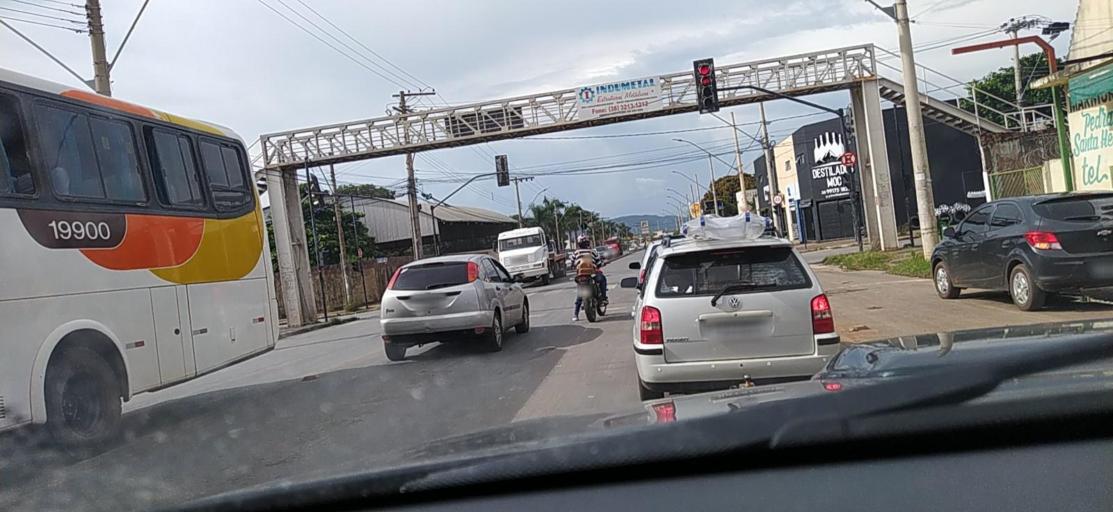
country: BR
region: Minas Gerais
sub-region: Montes Claros
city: Montes Claros
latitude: -16.7358
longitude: -43.8462
